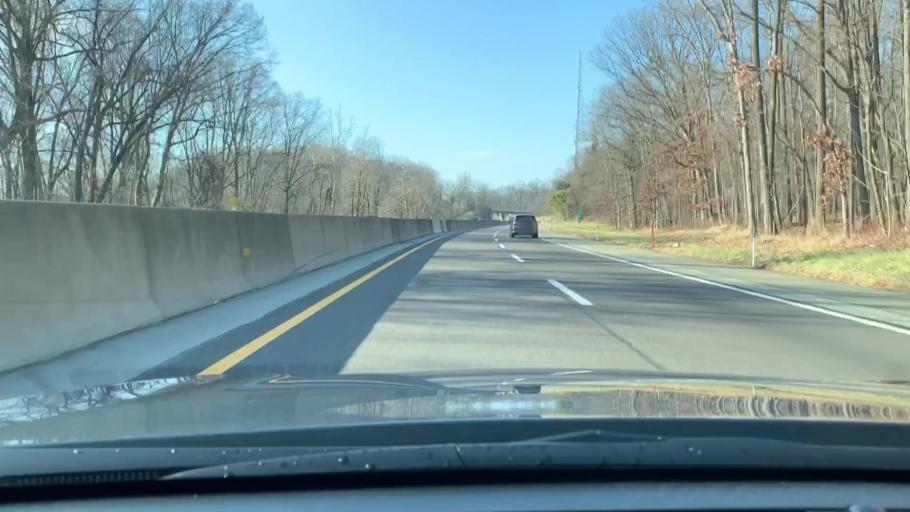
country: US
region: Pennsylvania
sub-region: Chester County
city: Chester Springs
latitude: 40.0702
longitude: -75.5645
